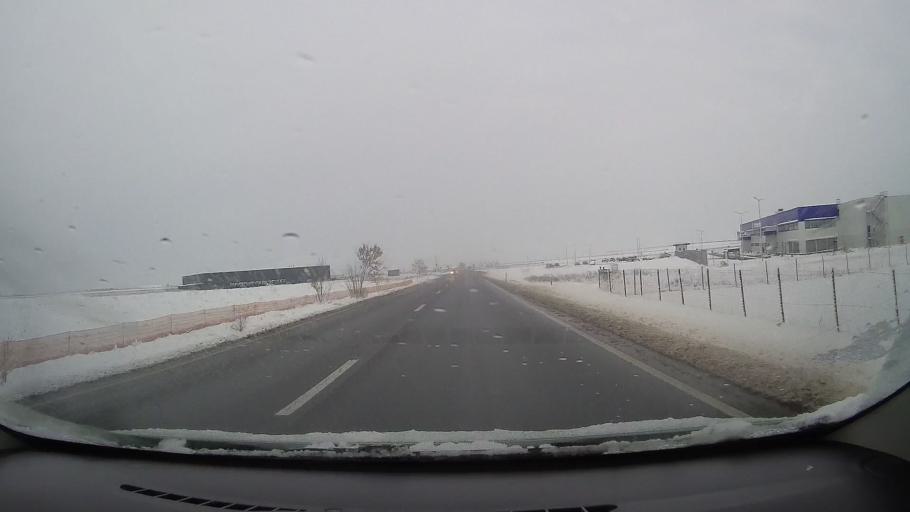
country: RO
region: Alba
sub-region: Municipiul Sebes
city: Lancram
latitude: 45.9641
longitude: 23.5327
